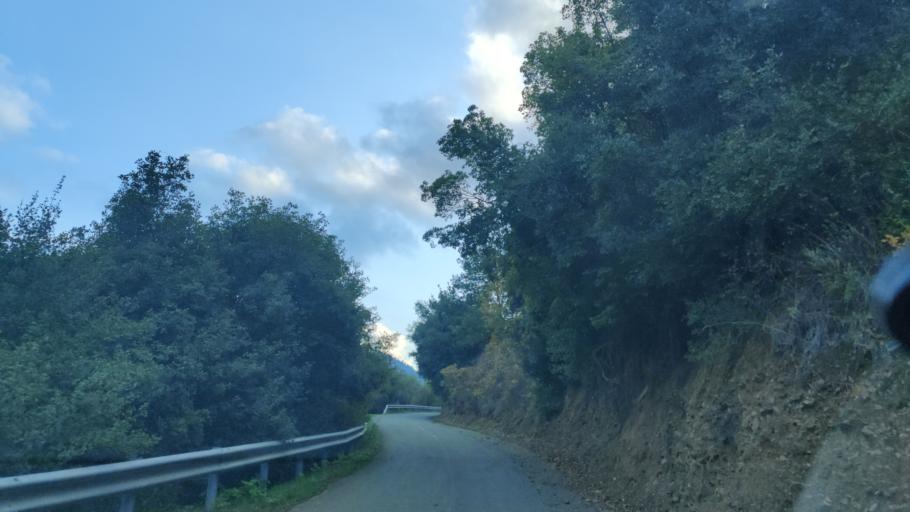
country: CY
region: Lefkosia
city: Lefka
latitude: 35.0472
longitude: 32.7356
